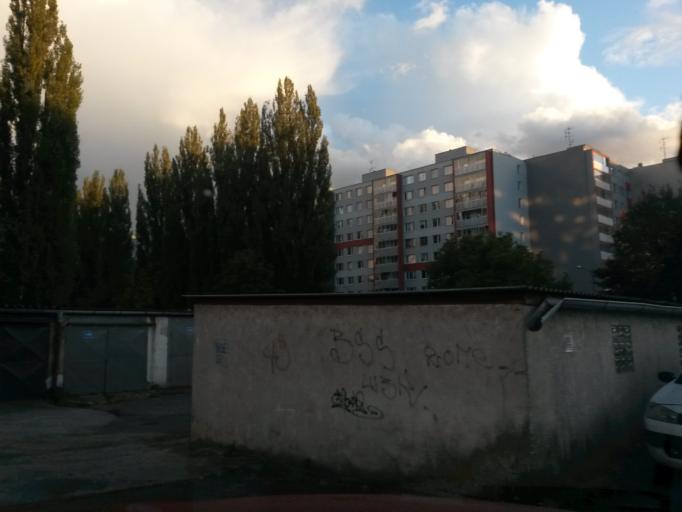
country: SK
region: Kosicky
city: Kosice
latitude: 48.6865
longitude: 21.2897
